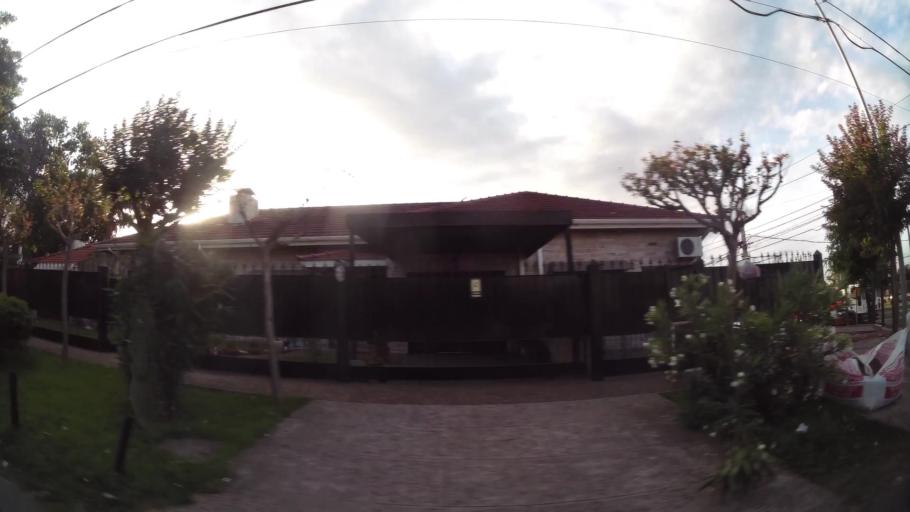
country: AR
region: Buenos Aires
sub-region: Partido de Tigre
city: Tigre
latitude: -34.4515
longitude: -58.6571
